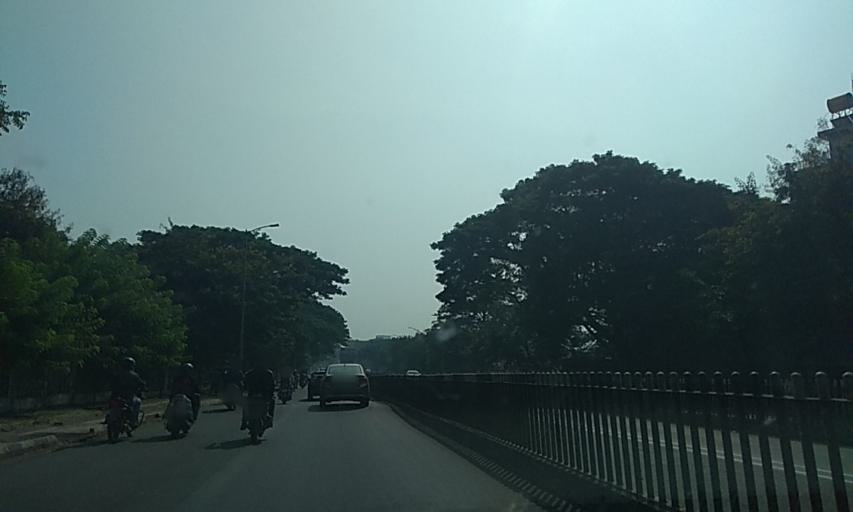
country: IN
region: Maharashtra
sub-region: Pune Division
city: Shivaji Nagar
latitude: 18.5468
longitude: 73.8742
